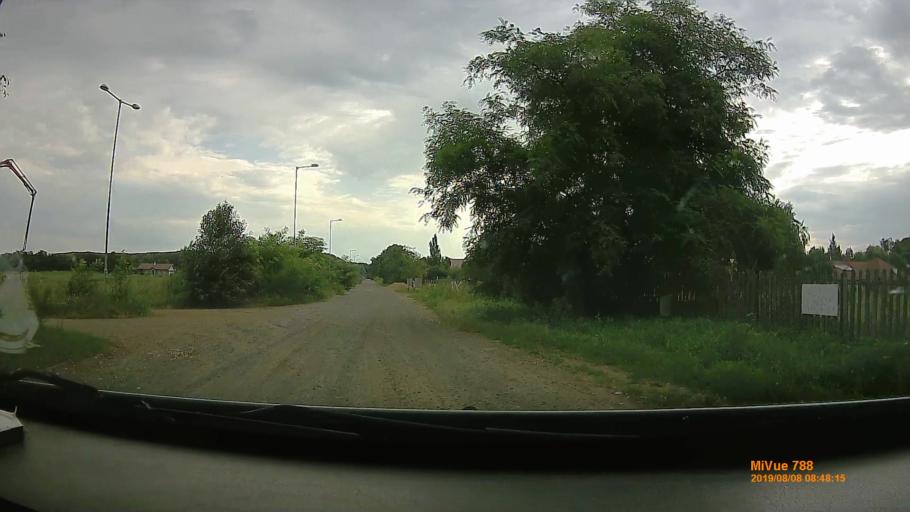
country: HU
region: Hajdu-Bihar
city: Debrecen
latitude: 47.5973
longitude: 21.6396
